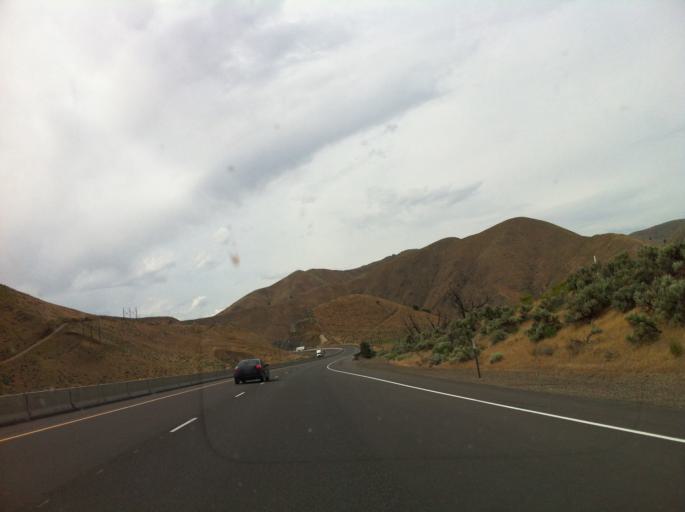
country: US
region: Idaho
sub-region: Washington County
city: Weiser
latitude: 44.4340
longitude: -117.3205
